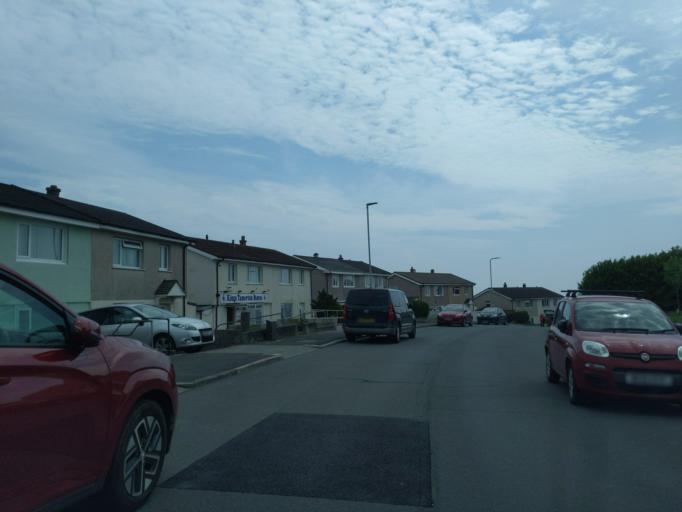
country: GB
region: England
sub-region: Cornwall
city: Torpoint
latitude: 50.4078
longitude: -4.1710
